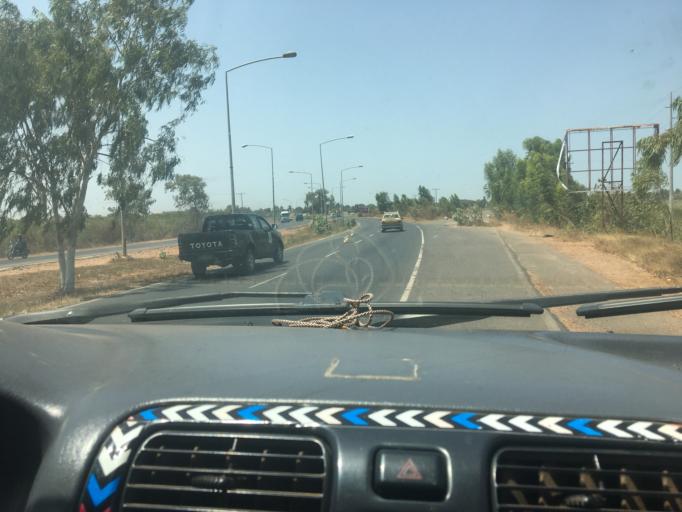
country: GM
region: Banjul
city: Bakau
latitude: 13.4659
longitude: -16.6542
